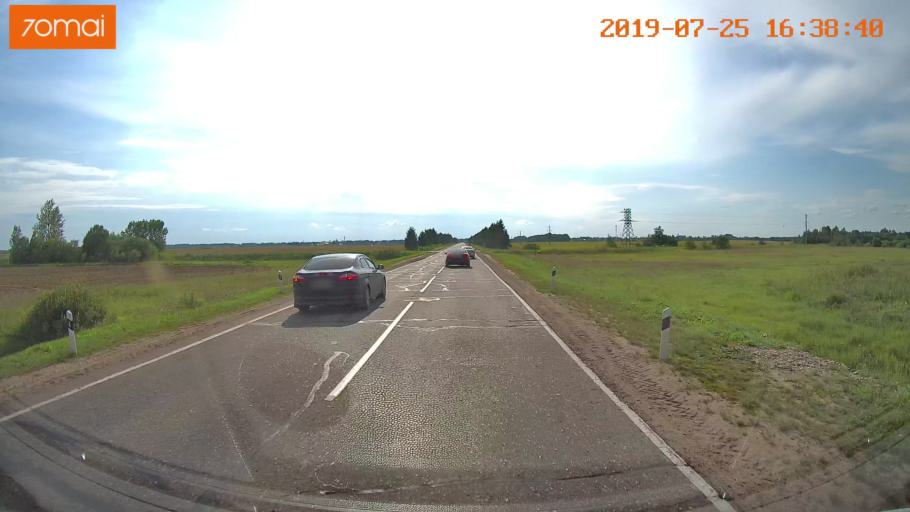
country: RU
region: Ivanovo
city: Privolzhsk
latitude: 57.3875
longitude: 41.3445
